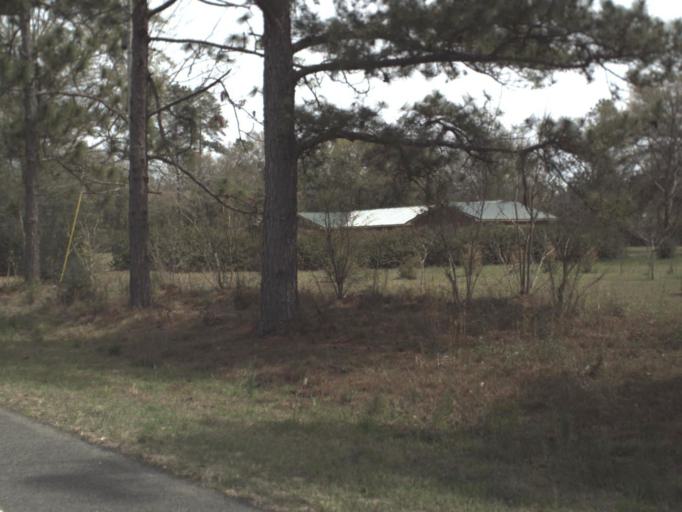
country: US
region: Alabama
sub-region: Geneva County
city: Geneva
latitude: 30.9343
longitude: -85.9606
